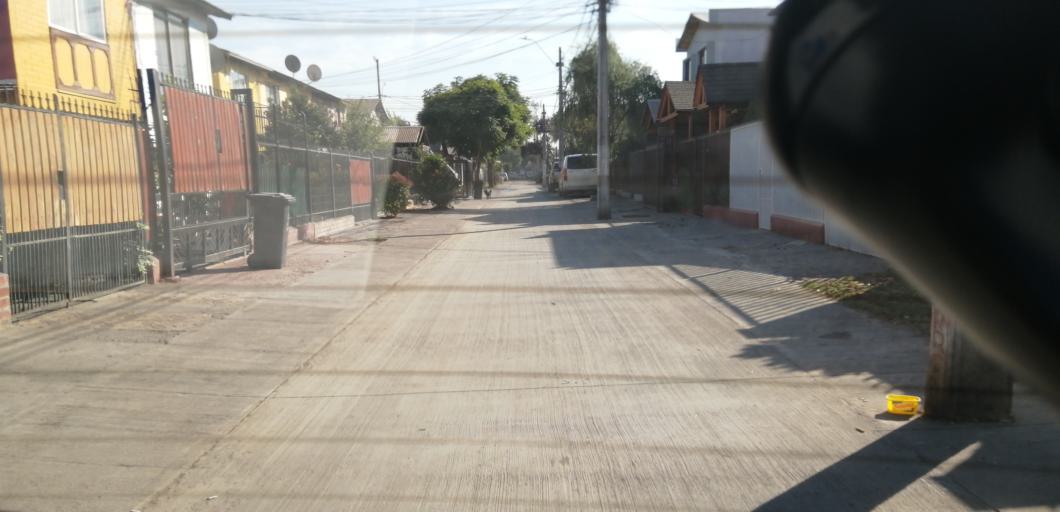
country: CL
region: Santiago Metropolitan
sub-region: Provincia de Santiago
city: Lo Prado
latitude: -33.4591
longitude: -70.7425
